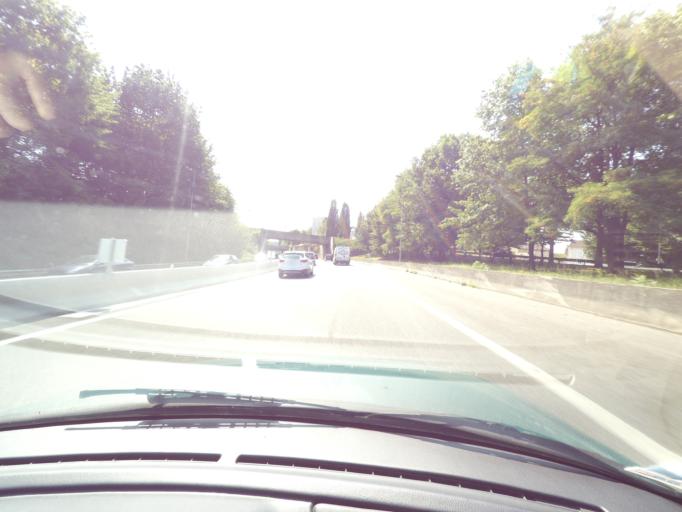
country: FR
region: Limousin
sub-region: Departement de la Haute-Vienne
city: Limoges
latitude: 45.8291
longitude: 1.2821
